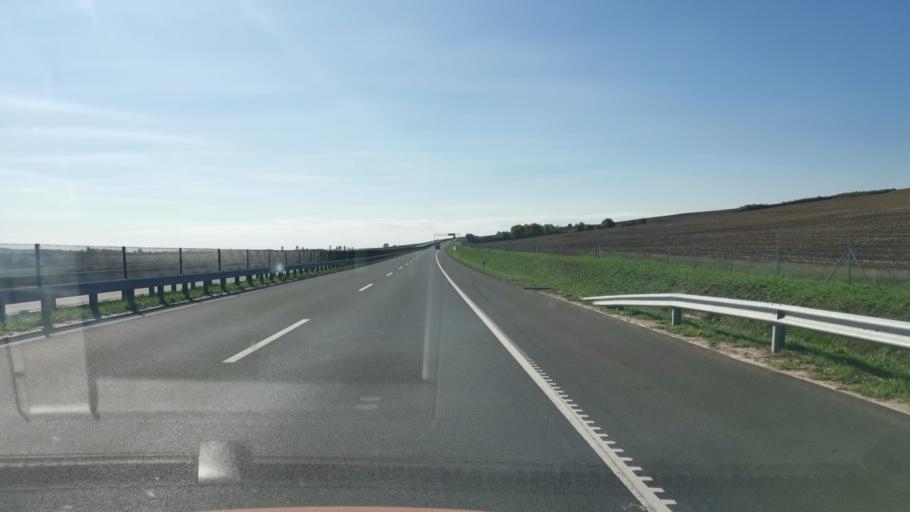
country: HU
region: Borsod-Abauj-Zemplen
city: Halmaj
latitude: 48.2720
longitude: 21.0000
